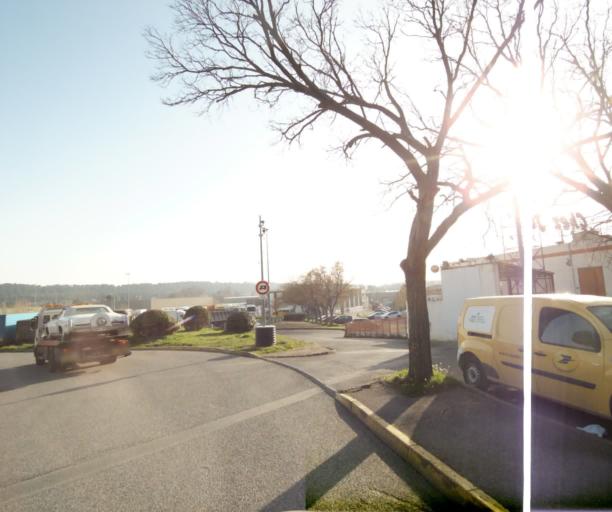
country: FR
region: Provence-Alpes-Cote d'Azur
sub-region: Departement des Bouches-du-Rhone
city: Saint-Victoret
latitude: 43.4204
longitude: 5.2682
